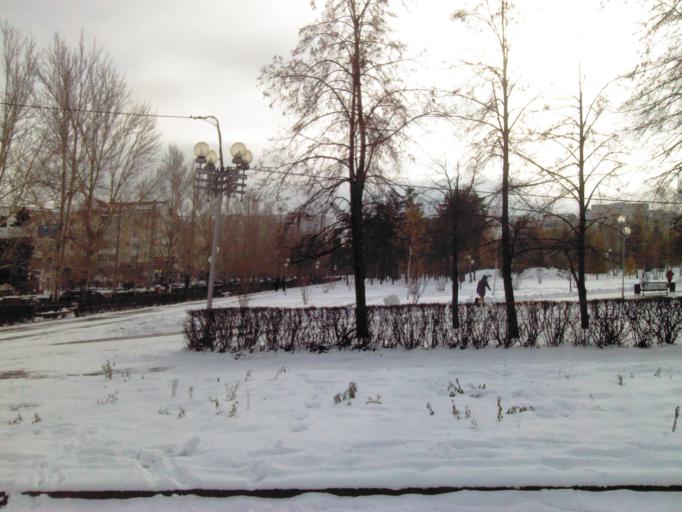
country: RU
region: Chelyabinsk
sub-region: Gorod Chelyabinsk
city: Chelyabinsk
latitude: 55.1626
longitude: 61.3928
